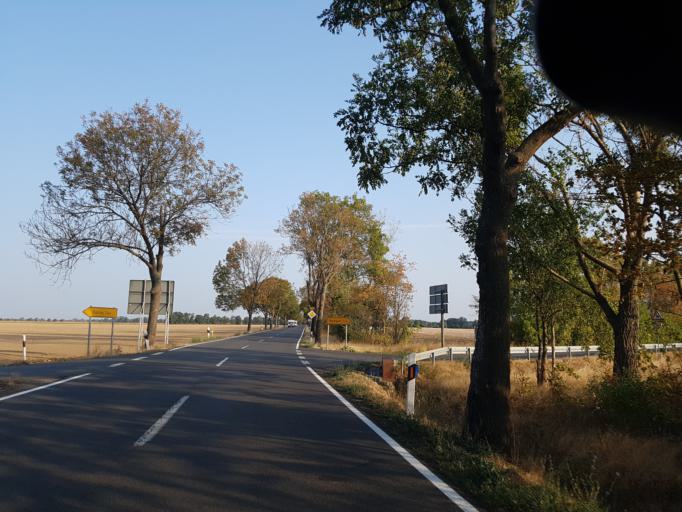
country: DE
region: Saxony-Anhalt
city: Muhlanger
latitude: 51.7866
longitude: 12.7097
